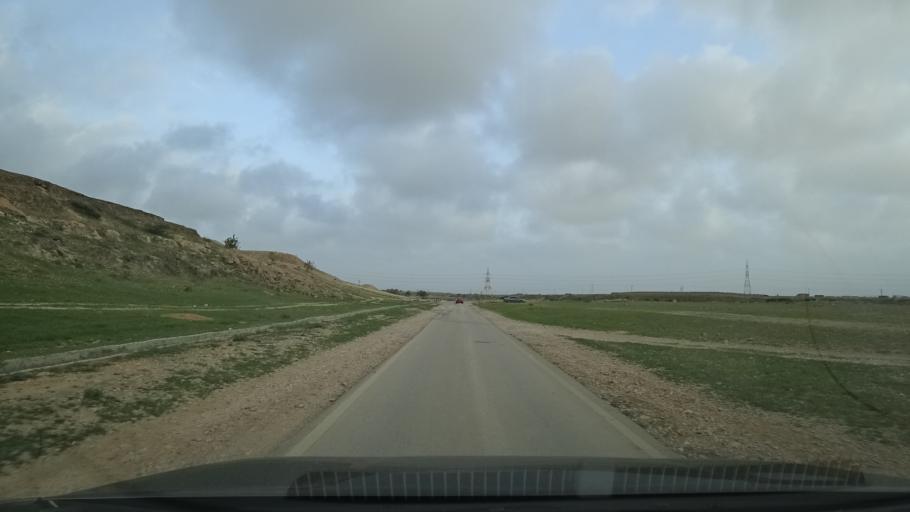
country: OM
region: Zufar
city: Salalah
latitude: 17.1097
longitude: 54.2284
